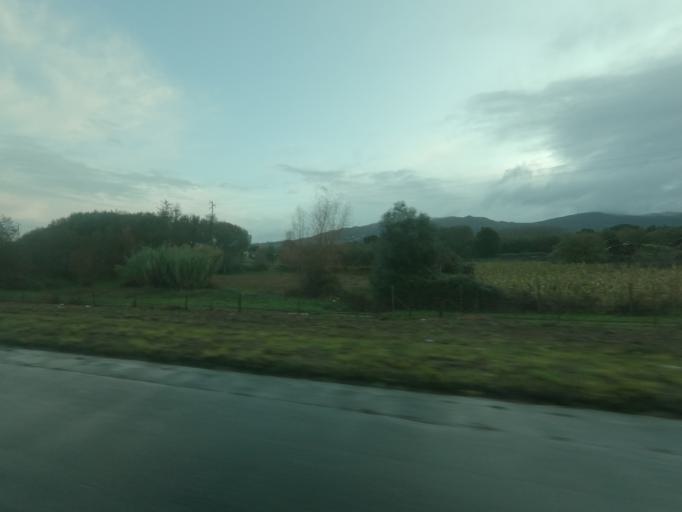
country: PT
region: Viana do Castelo
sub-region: Valenca
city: Valenza
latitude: 42.0047
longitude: -8.6459
